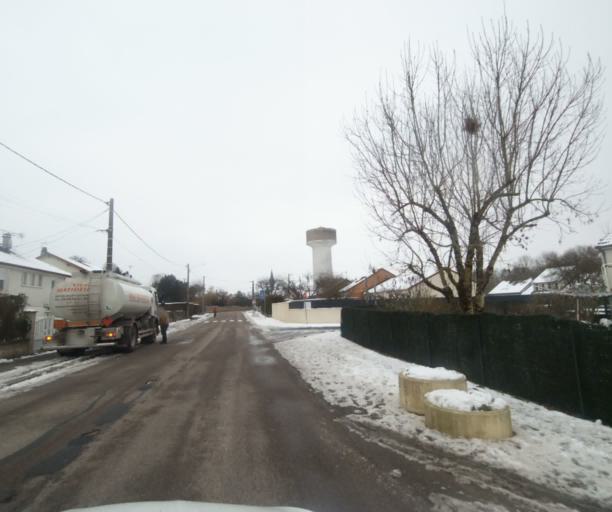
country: FR
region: Champagne-Ardenne
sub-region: Departement de la Haute-Marne
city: Villiers-en-Lieu
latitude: 48.5915
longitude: 4.8616
